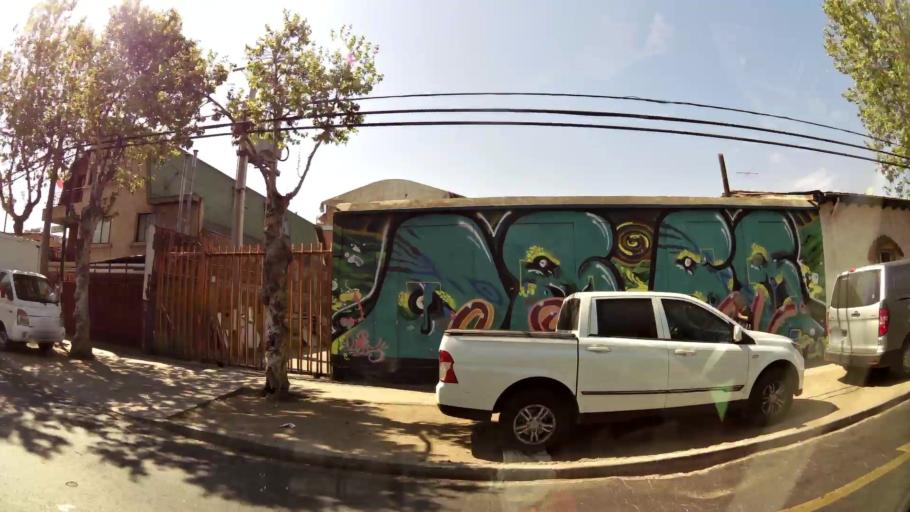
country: CL
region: Santiago Metropolitan
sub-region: Provincia de Maipo
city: San Bernardo
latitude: -33.5935
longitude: -70.7071
